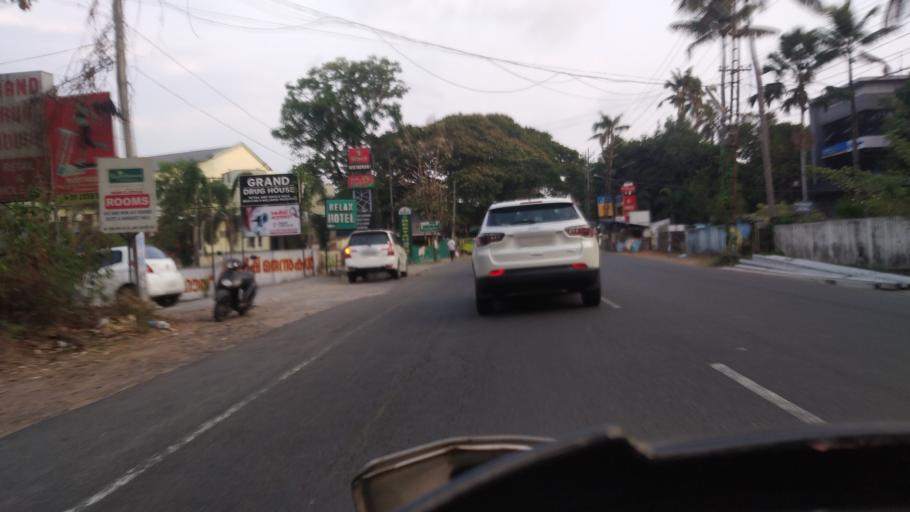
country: IN
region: Kerala
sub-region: Thrissur District
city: Kodungallur
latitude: 10.2355
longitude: 76.1941
